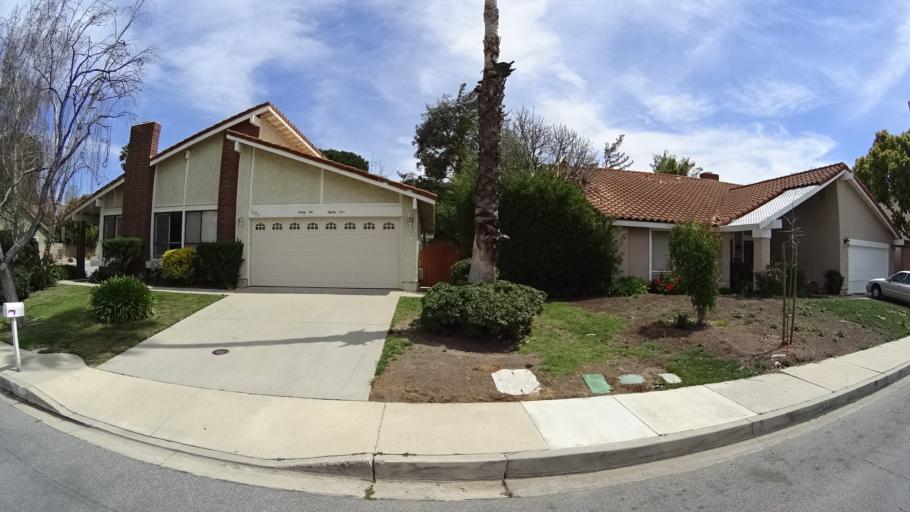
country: US
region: California
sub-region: Ventura County
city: Thousand Oaks
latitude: 34.1685
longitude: -118.8295
